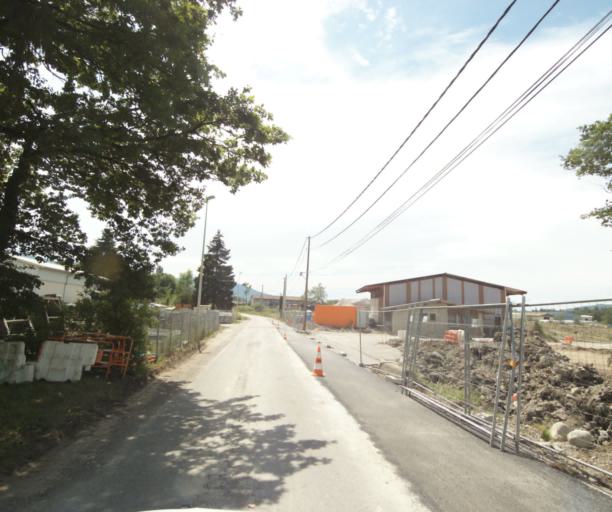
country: FR
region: Rhone-Alpes
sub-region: Departement de la Haute-Savoie
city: Perrignier
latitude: 46.3067
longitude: 6.4285
